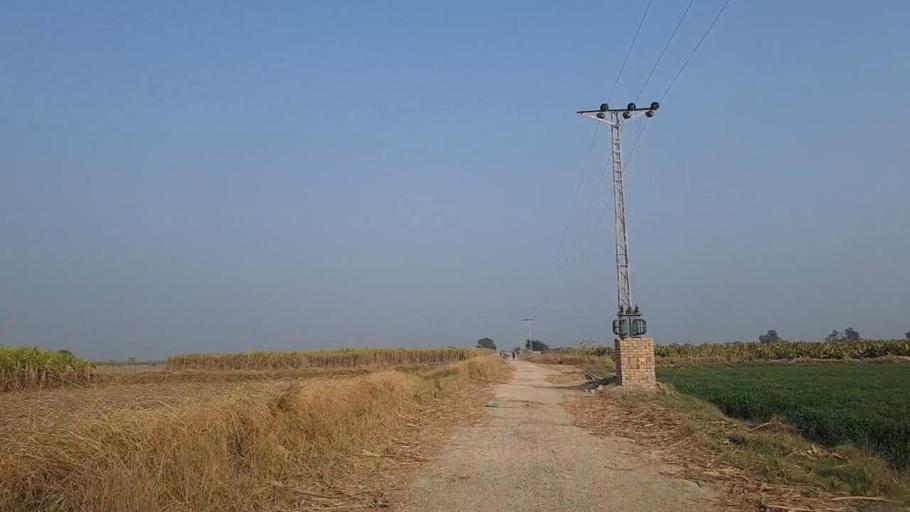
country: PK
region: Sindh
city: Sann
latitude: 26.1122
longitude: 68.1681
